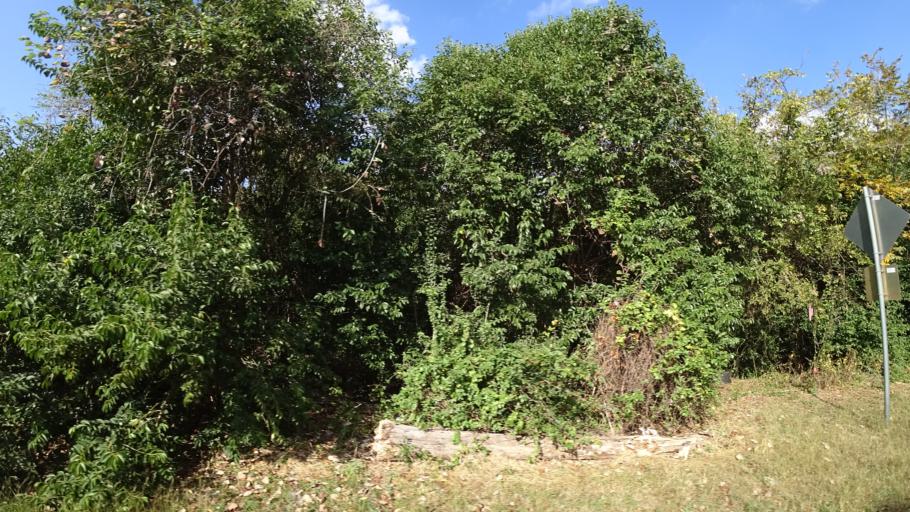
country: US
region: Texas
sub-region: Williamson County
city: Round Rock
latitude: 30.5037
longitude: -97.6781
